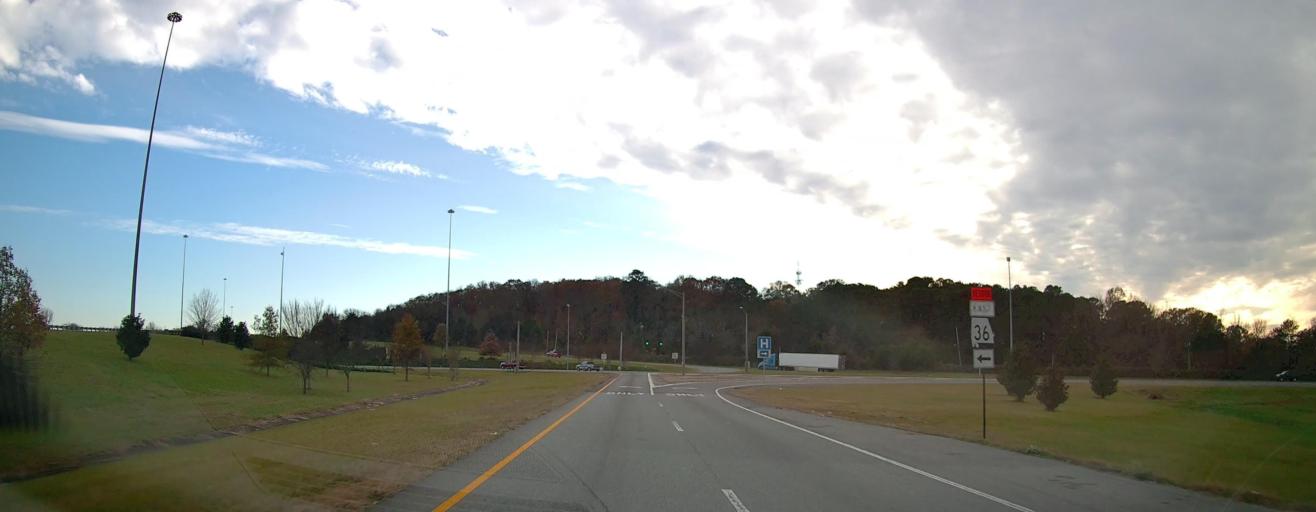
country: US
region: Alabama
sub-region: Morgan County
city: Priceville
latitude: 34.5355
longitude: -86.9066
